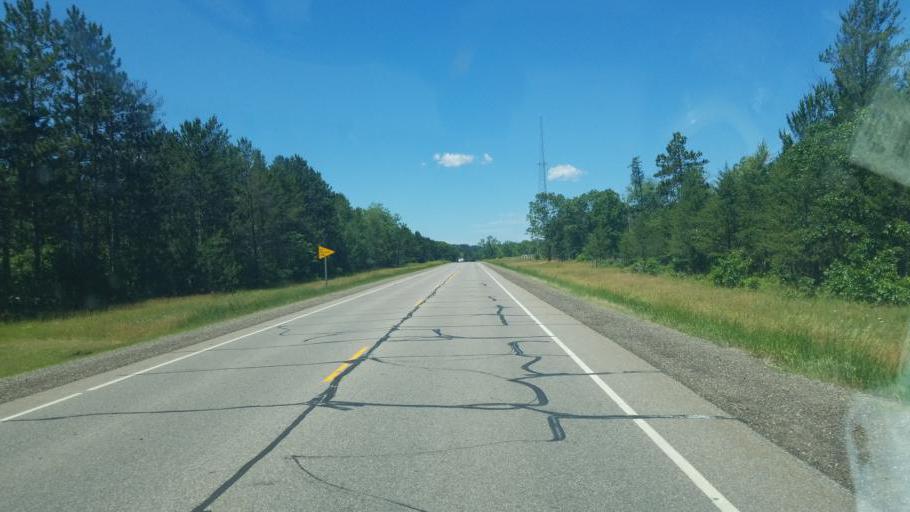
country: US
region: Wisconsin
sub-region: Adams County
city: Friendship
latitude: 44.0469
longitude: -89.9781
